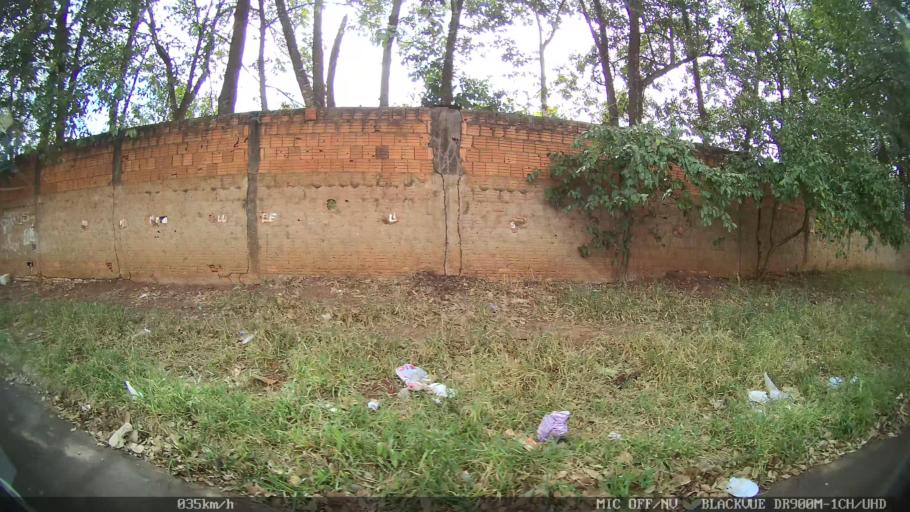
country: BR
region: Sao Paulo
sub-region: Catanduva
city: Catanduva
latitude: -21.1581
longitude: -48.9722
